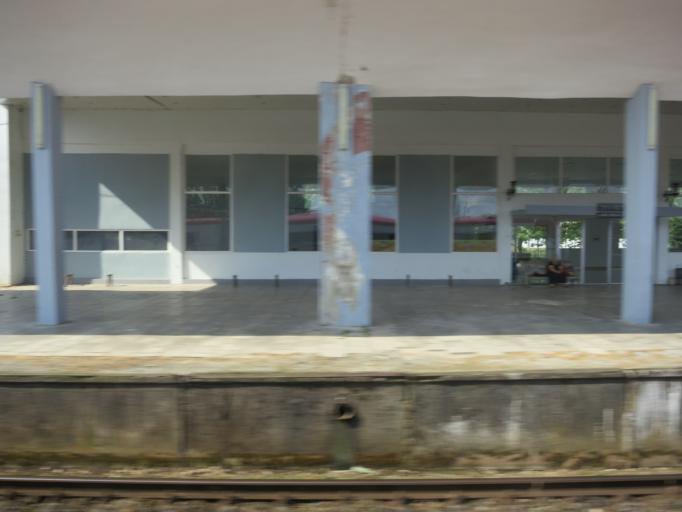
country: GE
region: Guria
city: Lanchkhuti
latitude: 42.0920
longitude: 42.0437
